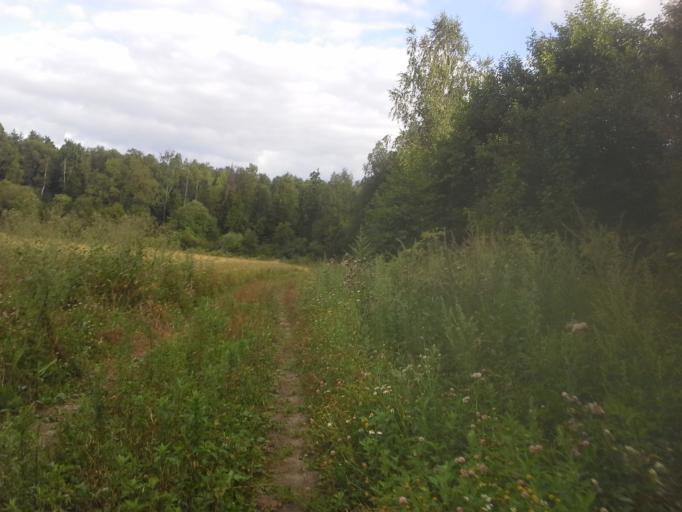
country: RU
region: Moskovskaya
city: Kievskij
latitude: 55.4483
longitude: 36.8623
